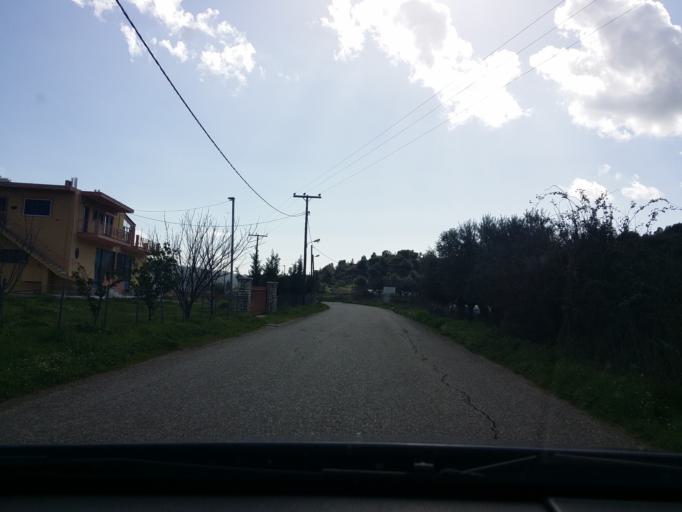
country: GR
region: West Greece
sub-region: Nomos Aitolias kai Akarnanias
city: Astakos
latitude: 38.5669
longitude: 21.0951
